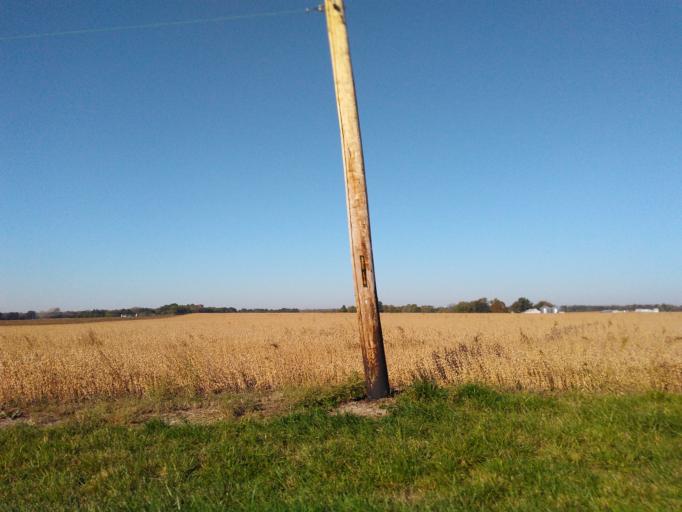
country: US
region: Illinois
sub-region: Madison County
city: Saint Jacob
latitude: 38.7412
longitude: -89.8006
